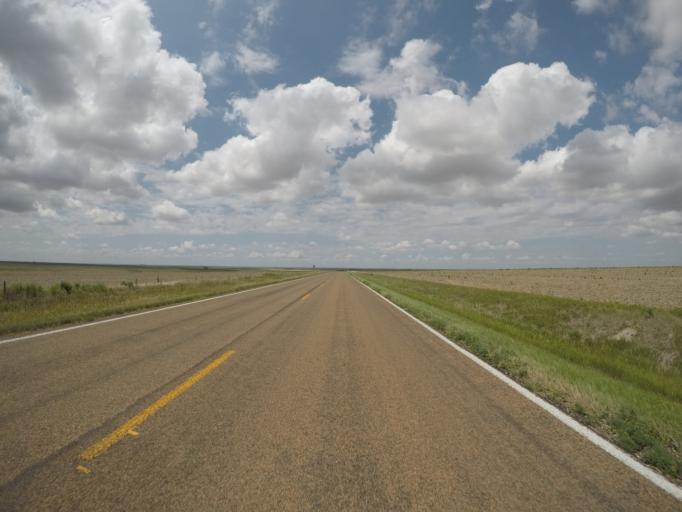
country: US
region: Kansas
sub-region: Rawlins County
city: Atwood
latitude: 39.9051
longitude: -101.0494
